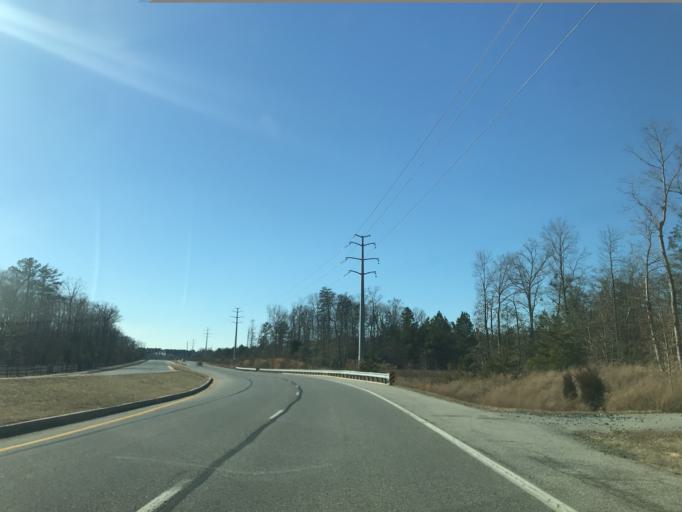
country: US
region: Maryland
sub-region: Charles County
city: La Plata
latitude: 38.5602
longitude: -76.9629
